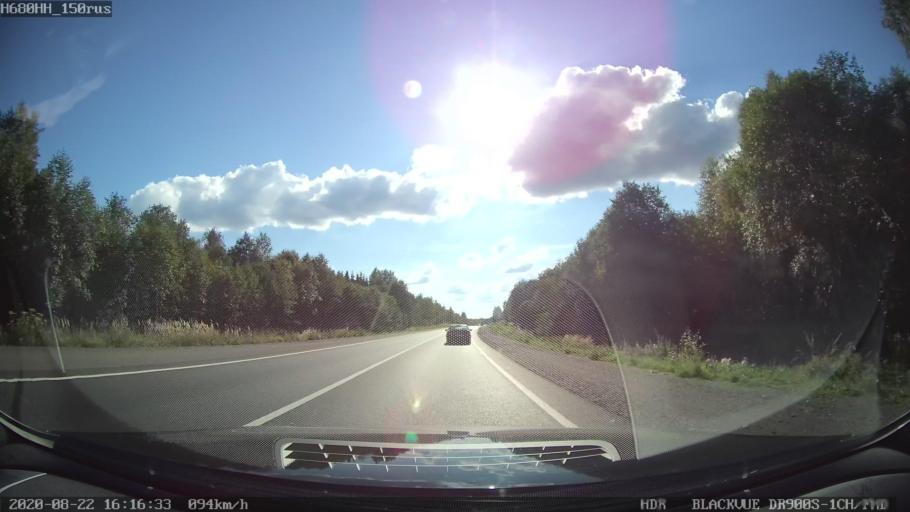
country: RU
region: Tverskaya
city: Rameshki
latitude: 57.4326
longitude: 36.1770
